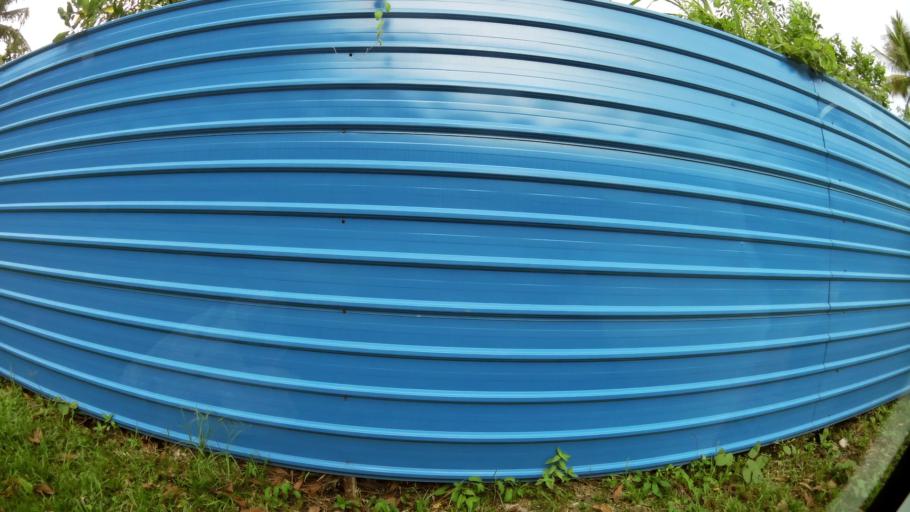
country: BN
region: Brunei and Muara
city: Bandar Seri Begawan
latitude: 4.9241
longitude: 115.0117
